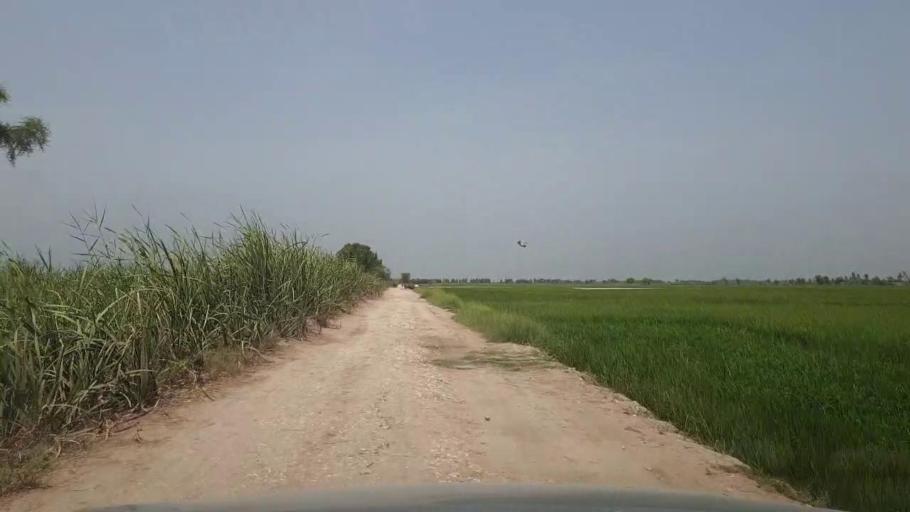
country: PK
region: Sindh
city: Garhi Yasin
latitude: 27.9361
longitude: 68.4315
